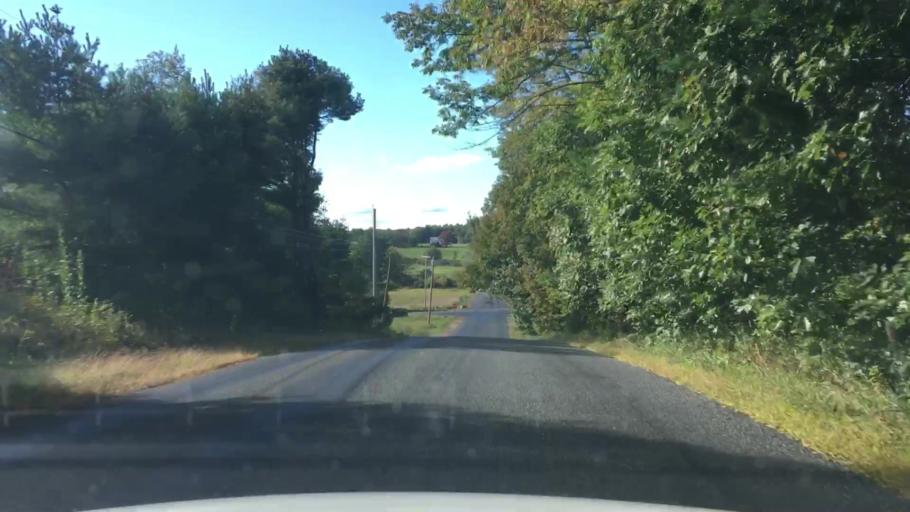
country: US
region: Maine
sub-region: Androscoggin County
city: Lisbon Falls
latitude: 43.9624
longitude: -70.0583
